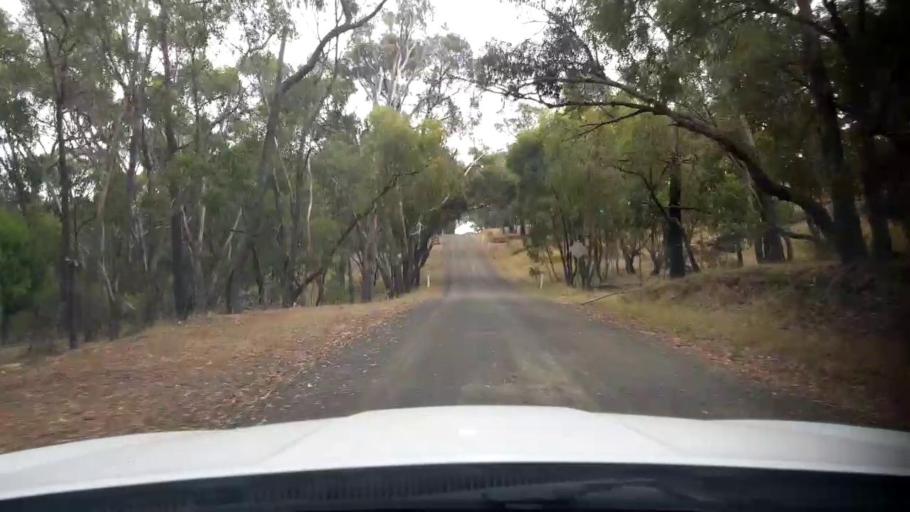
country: AU
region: Victoria
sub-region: Whittlesea
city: Whittlesea
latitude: -37.4919
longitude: 145.0514
